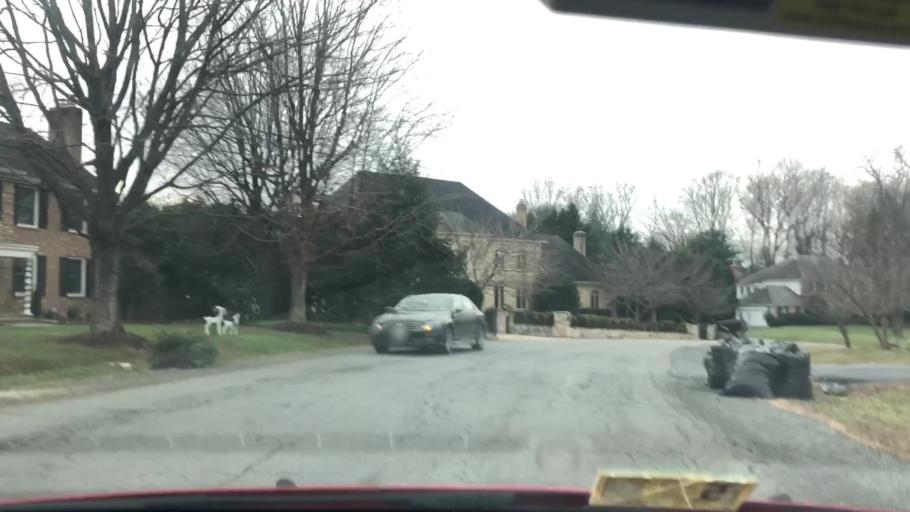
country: US
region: Virginia
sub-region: Fairfax County
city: Wolf Trap
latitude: 38.9669
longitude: -77.2729
